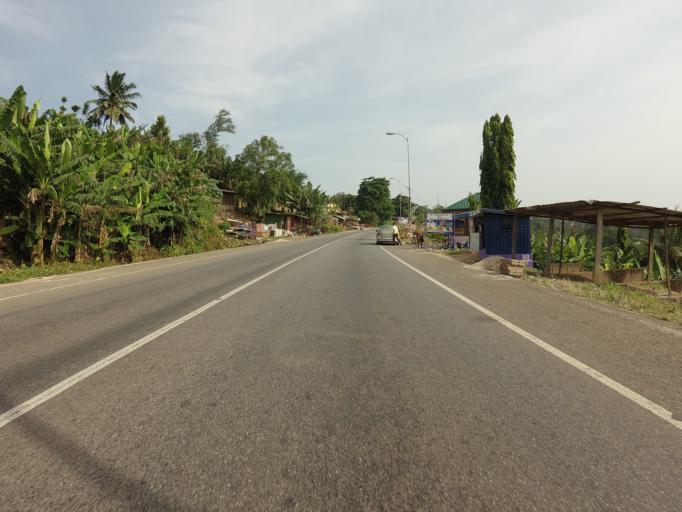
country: GH
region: Eastern
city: Aburi
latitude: 5.8443
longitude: -0.1740
